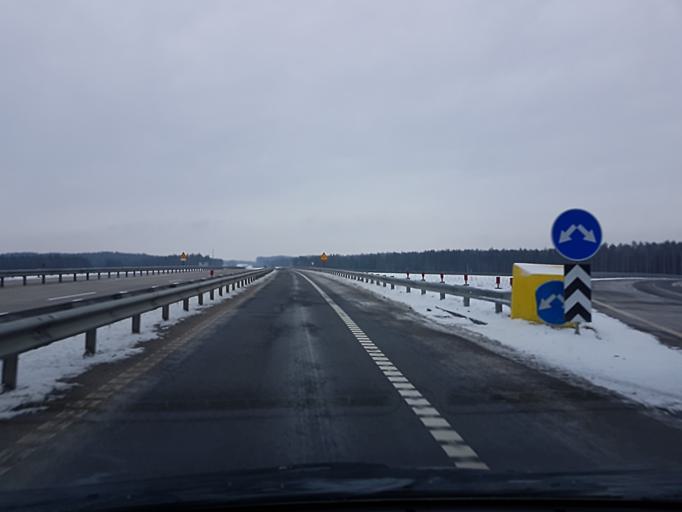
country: BY
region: Minsk
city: Rakaw
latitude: 53.9627
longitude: 27.0866
